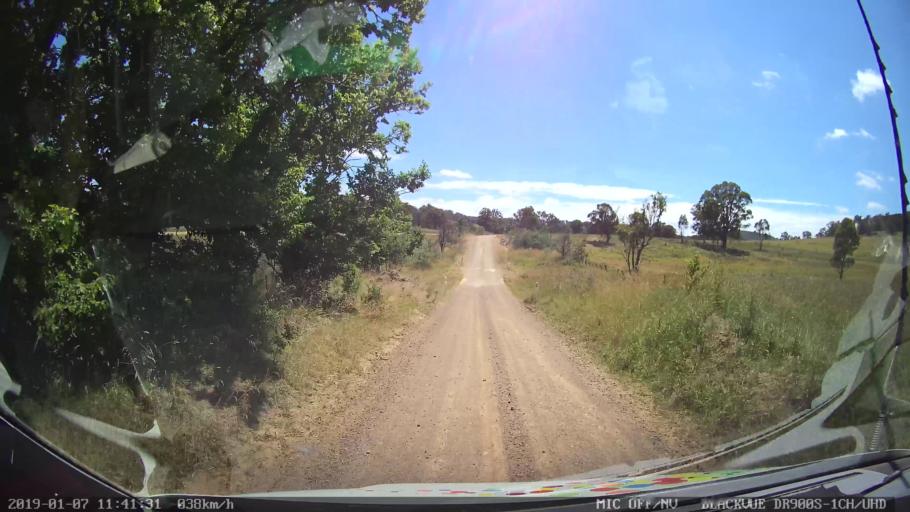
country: AU
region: New South Wales
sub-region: Guyra
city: Guyra
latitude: -30.3601
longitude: 151.5889
